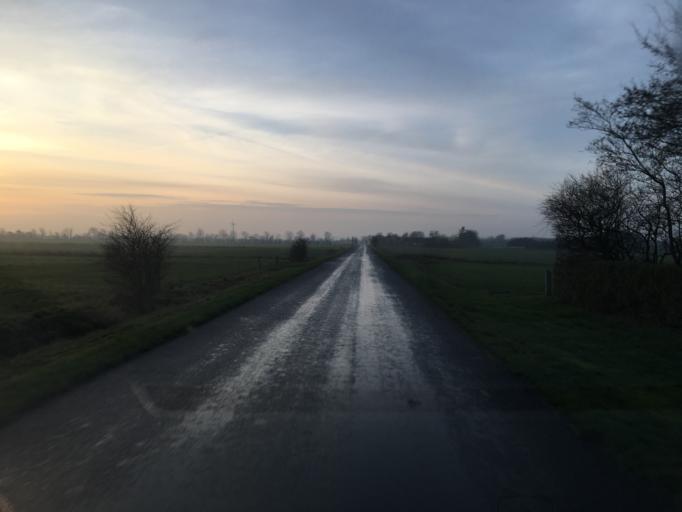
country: DK
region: South Denmark
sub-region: Tonder Kommune
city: Logumkloster
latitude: 55.1106
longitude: 9.0007
